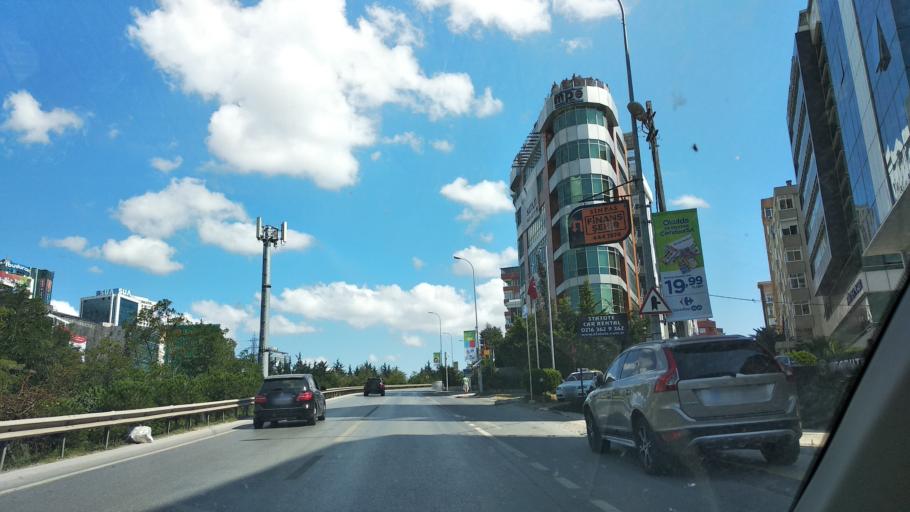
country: TR
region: Istanbul
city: Umraniye
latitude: 40.9966
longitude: 29.1358
